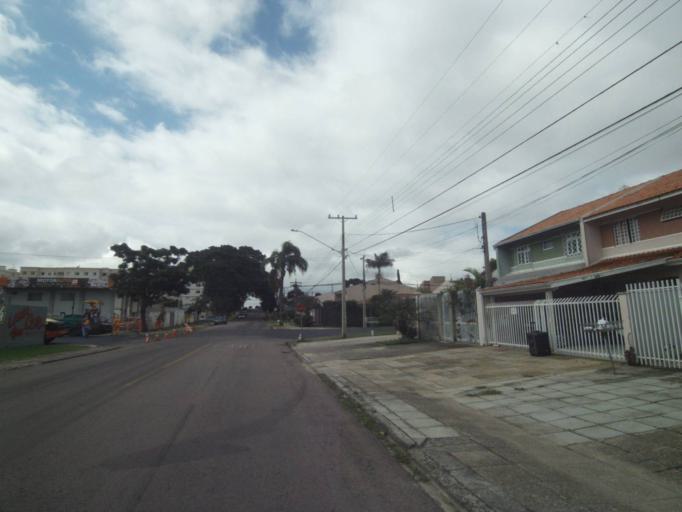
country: BR
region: Parana
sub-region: Pinhais
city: Pinhais
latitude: -25.4588
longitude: -49.2188
